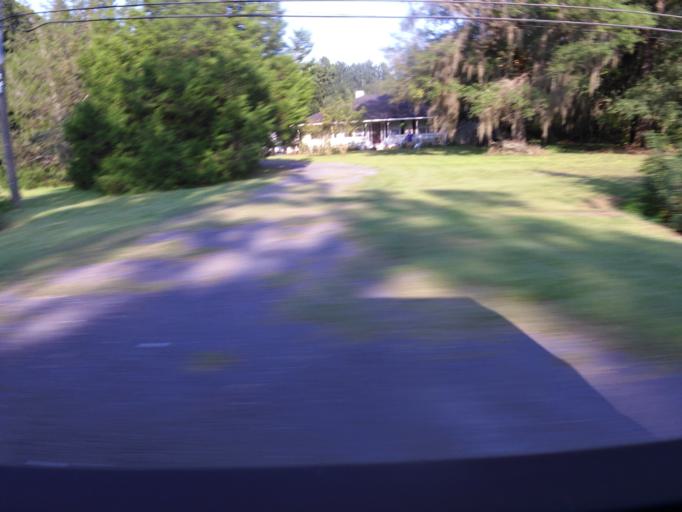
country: US
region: Florida
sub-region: Duval County
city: Baldwin
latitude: 30.3094
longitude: -82.0084
